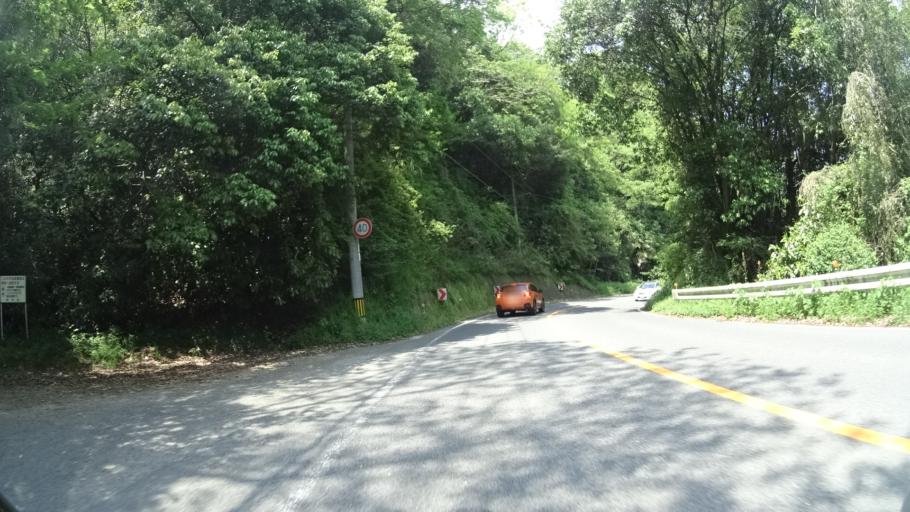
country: JP
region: Ehime
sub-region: Shikoku-chuo Shi
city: Matsuyama
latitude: 33.8864
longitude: 132.8360
